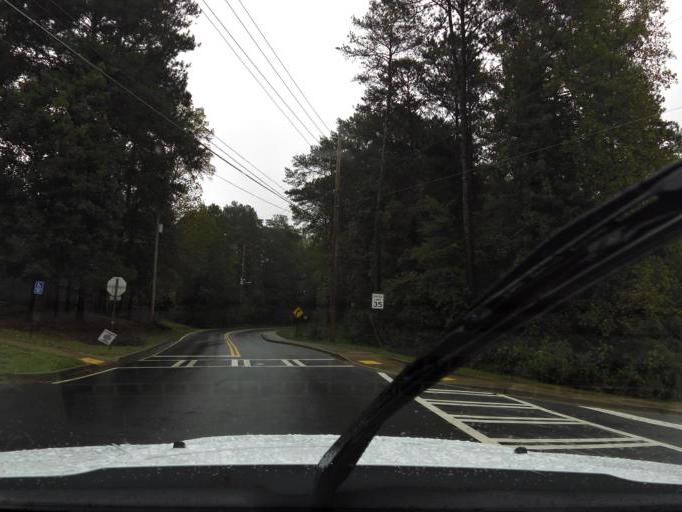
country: US
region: Georgia
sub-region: Cobb County
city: Acworth
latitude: 34.0539
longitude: -84.6611
